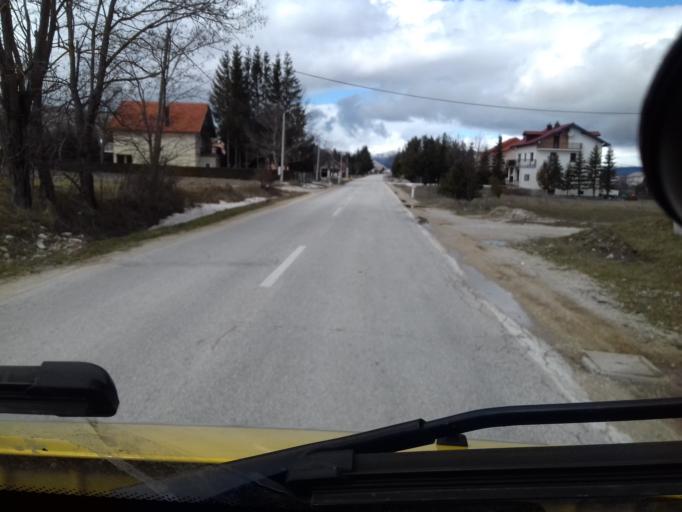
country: BA
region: Federation of Bosnia and Herzegovina
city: Tomislavgrad
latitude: 43.6266
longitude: 17.2519
